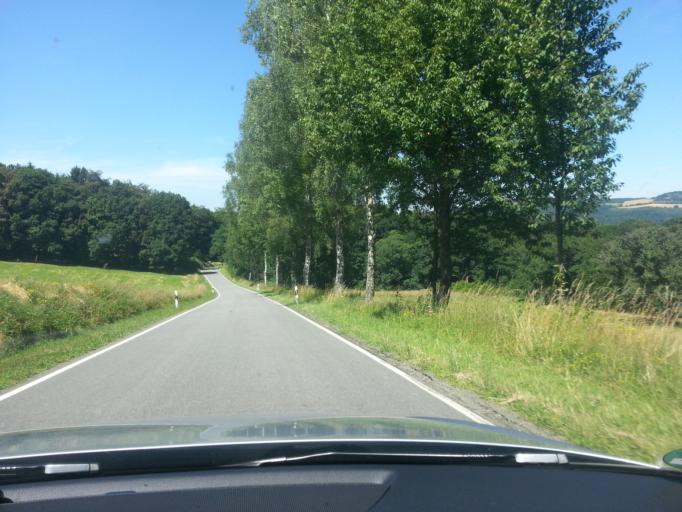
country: DE
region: Rheinland-Pfalz
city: Fockelberg
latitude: 49.5350
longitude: 7.4841
